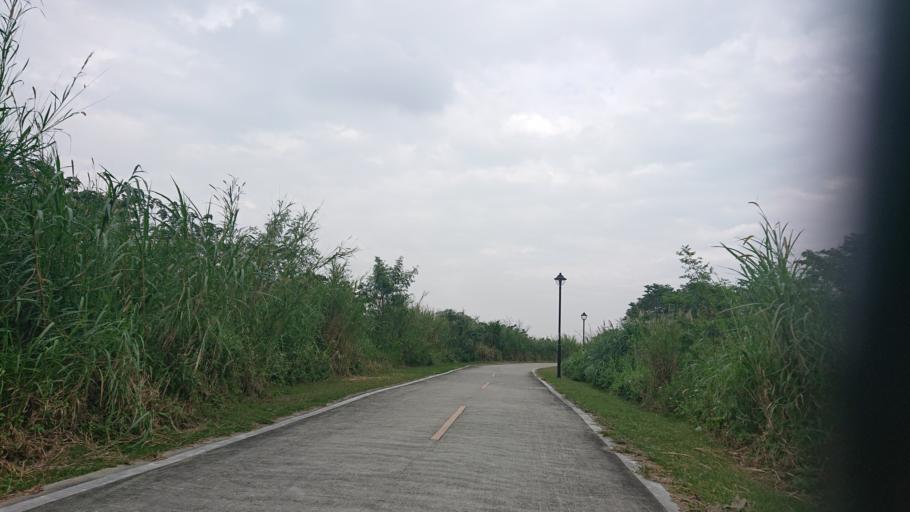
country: TW
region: Taiwan
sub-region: Taoyuan
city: Taoyuan
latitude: 24.9509
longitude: 121.3632
